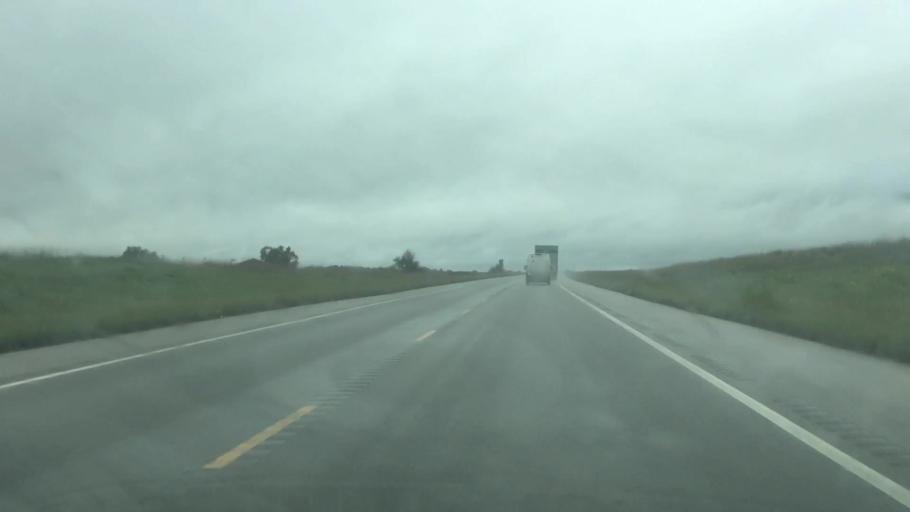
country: US
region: Kansas
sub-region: Allen County
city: Iola
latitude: 38.0890
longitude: -95.3644
